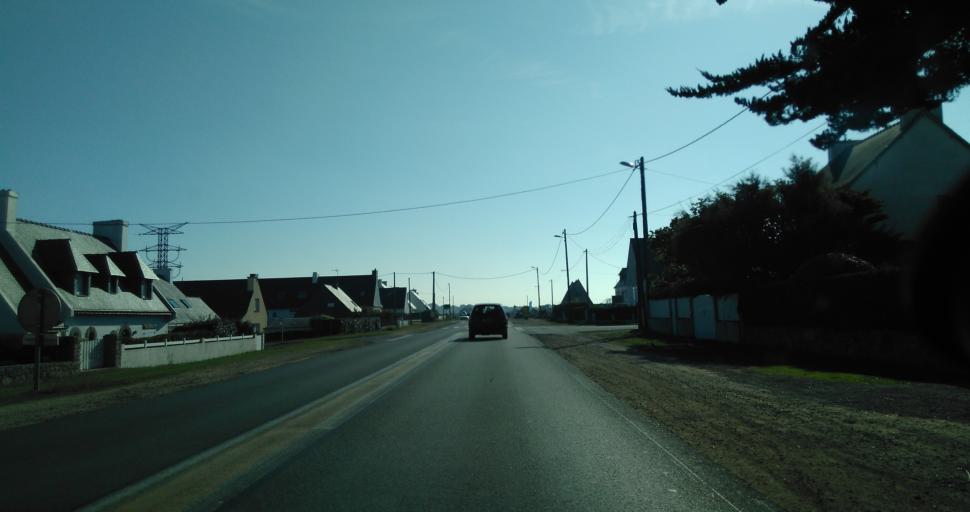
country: FR
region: Brittany
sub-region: Departement du Morbihan
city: Saint-Pierre-Quiberon
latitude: 47.5529
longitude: -3.1342
